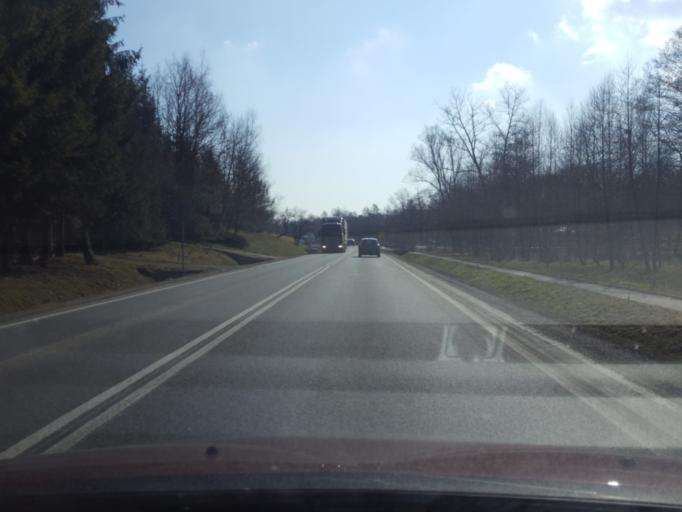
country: PL
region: Lesser Poland Voivodeship
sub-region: Powiat brzeski
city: Czchow
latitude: 49.8539
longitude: 20.6443
